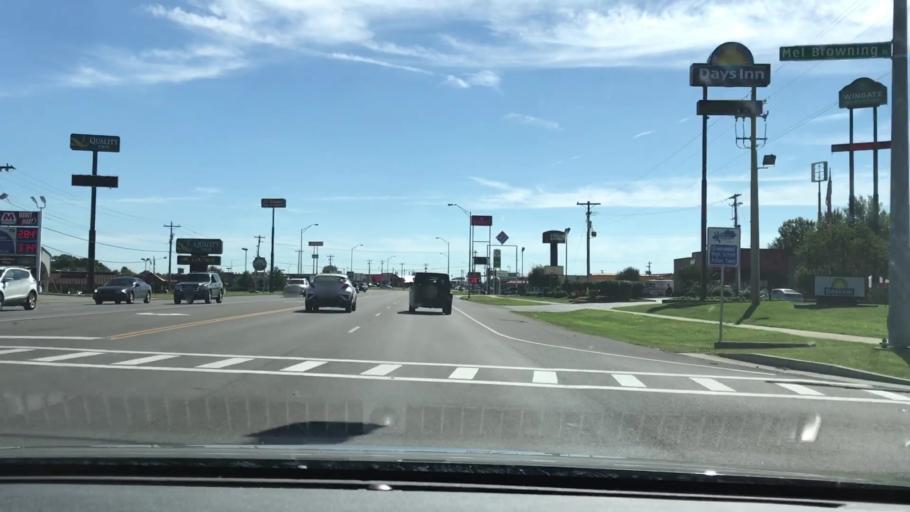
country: US
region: Kentucky
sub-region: Warren County
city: Plano
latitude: 36.9323
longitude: -86.4160
